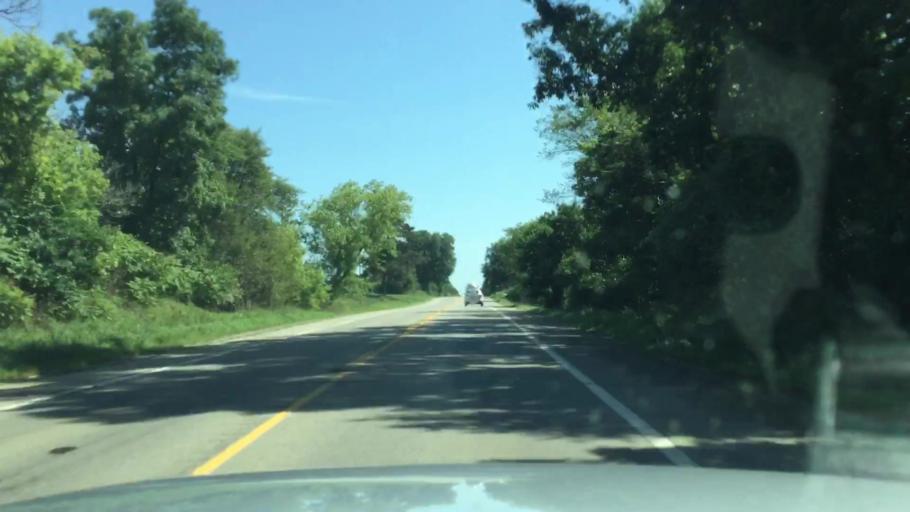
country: US
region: Michigan
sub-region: Lenawee County
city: Clinton
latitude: 42.0730
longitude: -84.0462
